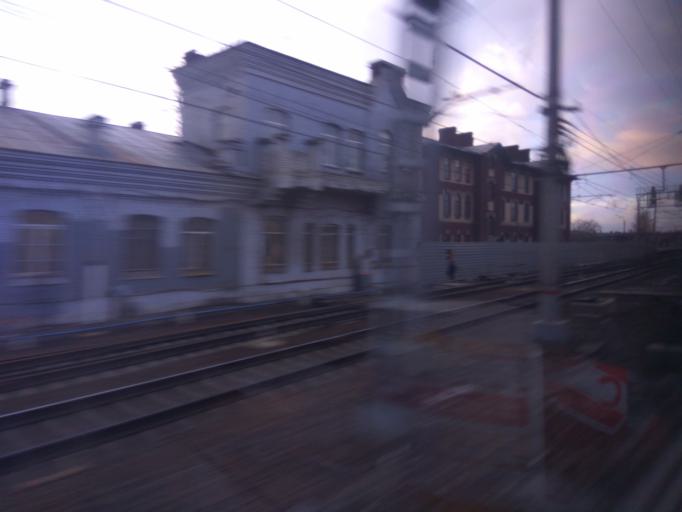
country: RU
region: St.-Petersburg
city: Centralniy
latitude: 59.9048
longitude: 30.3759
